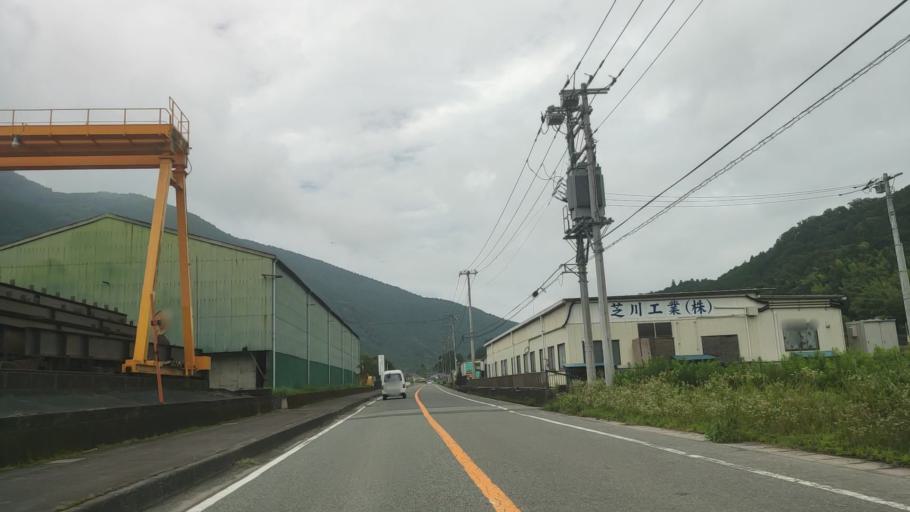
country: JP
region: Shizuoka
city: Fujinomiya
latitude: 35.2093
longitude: 138.5510
